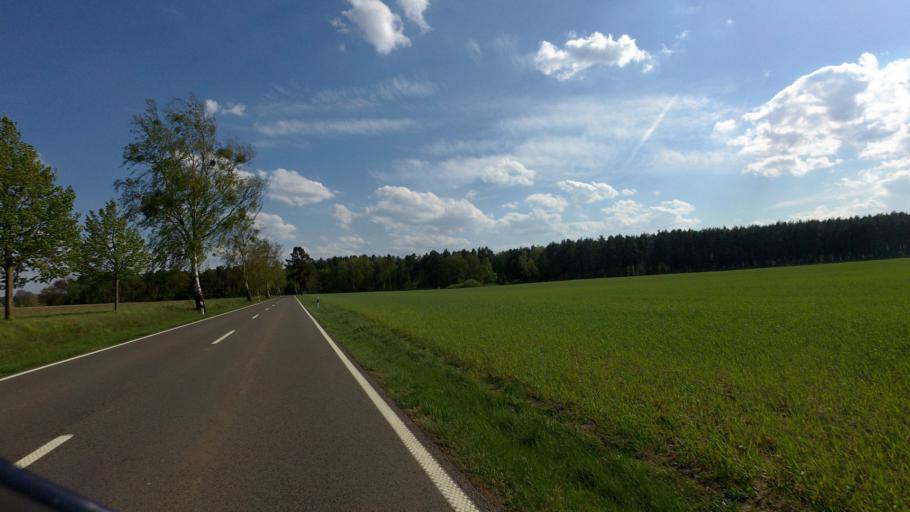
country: DE
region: Brandenburg
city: Templin
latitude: 53.0611
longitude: 13.5205
